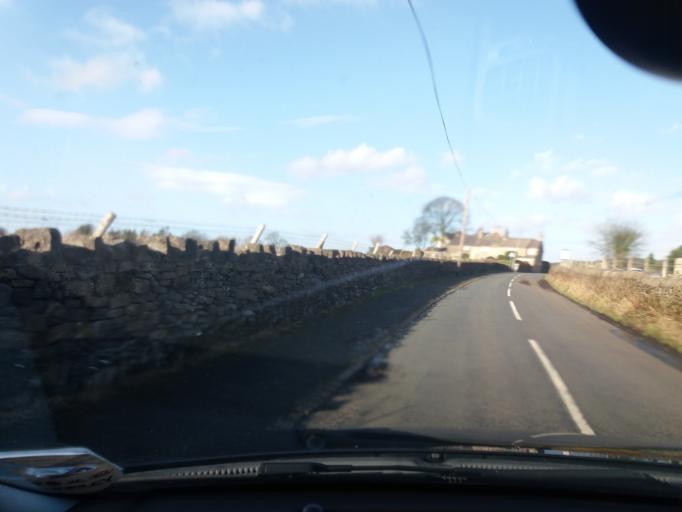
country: GB
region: England
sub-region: Lancashire
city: Adlington
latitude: 53.6329
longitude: -2.5812
